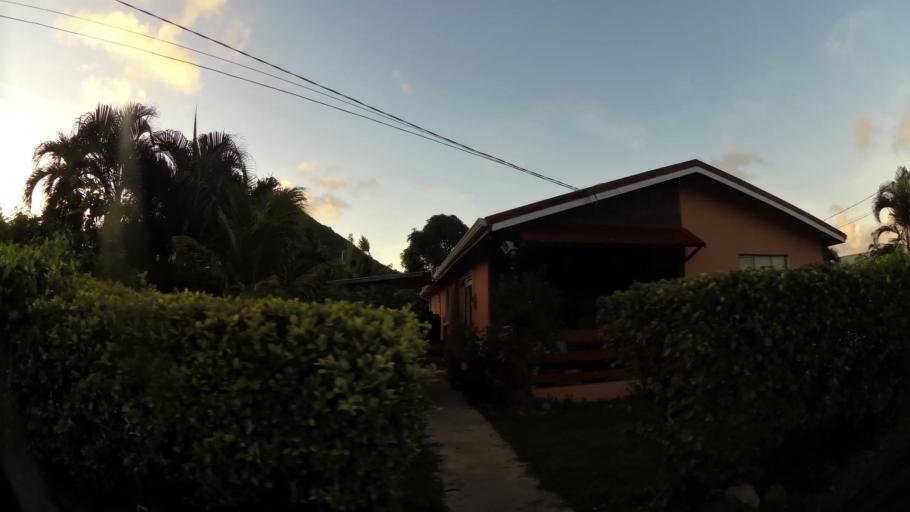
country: LC
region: Gros-Islet
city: Gros Islet
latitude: 14.0651
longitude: -60.9553
